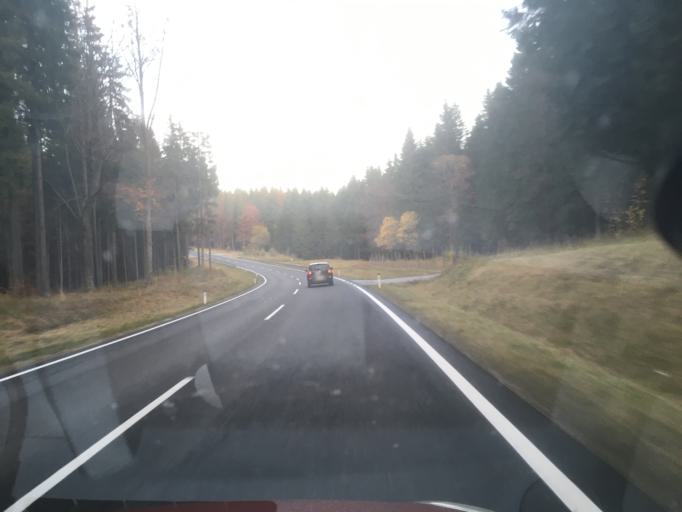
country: AT
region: Lower Austria
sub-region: Politischer Bezirk Zwettl
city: Langschlag
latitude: 48.5562
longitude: 14.7046
